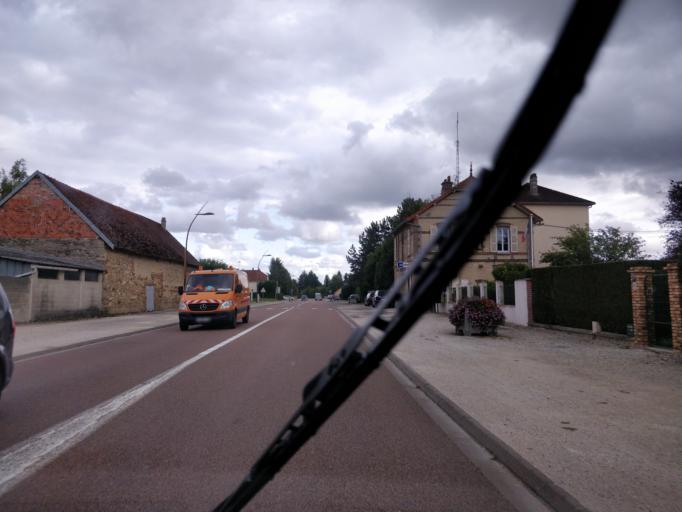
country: FR
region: Champagne-Ardenne
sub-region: Departement de l'Aube
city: Lusigny-sur-Barse
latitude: 48.2507
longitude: 4.2644
